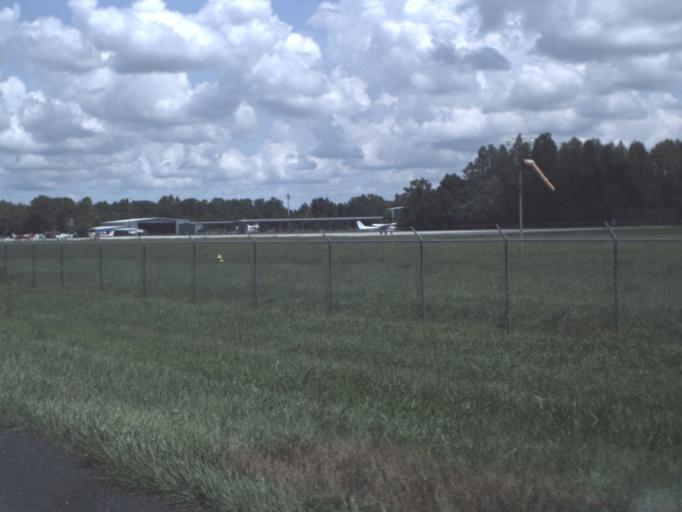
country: US
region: Florida
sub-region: Citrus County
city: Crystal River
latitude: 28.8675
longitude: -82.5796
